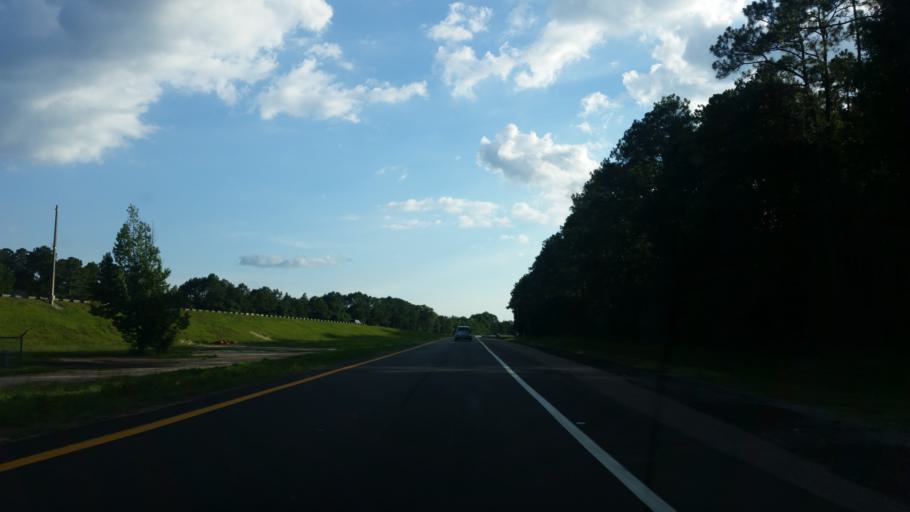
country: US
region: Florida
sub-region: Okaloosa County
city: Crestview
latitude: 30.6994
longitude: -86.7518
